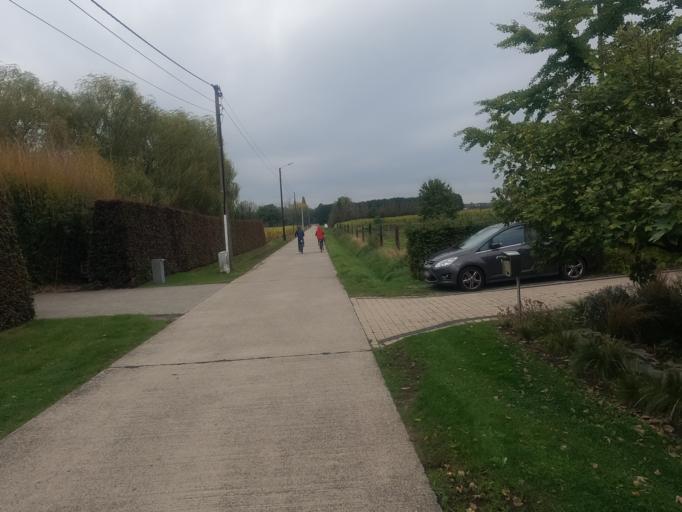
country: BE
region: Flanders
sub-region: Provincie Antwerpen
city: Heist-op-den-Berg
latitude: 51.1102
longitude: 4.7073
